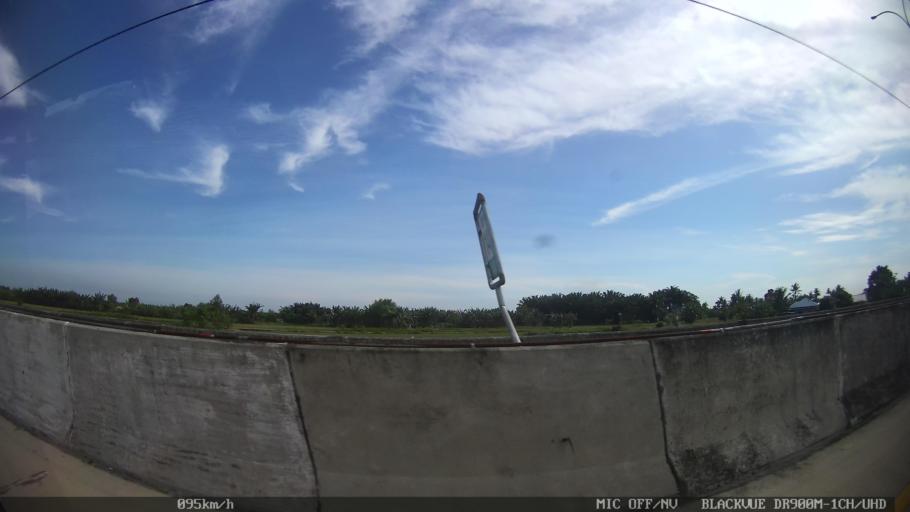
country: ID
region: North Sumatra
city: Sunggal
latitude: 3.6413
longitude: 98.5678
